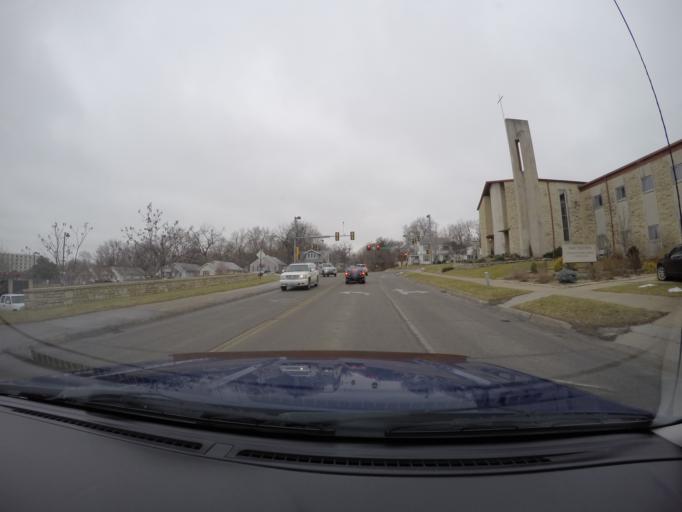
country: US
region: Kansas
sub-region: Riley County
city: Manhattan
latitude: 39.1866
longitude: -96.5855
